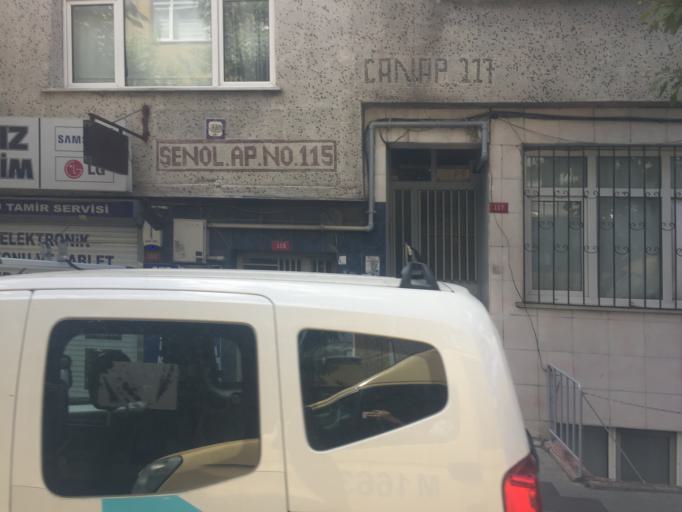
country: TR
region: Istanbul
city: Esenler
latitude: 41.0506
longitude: 28.9068
